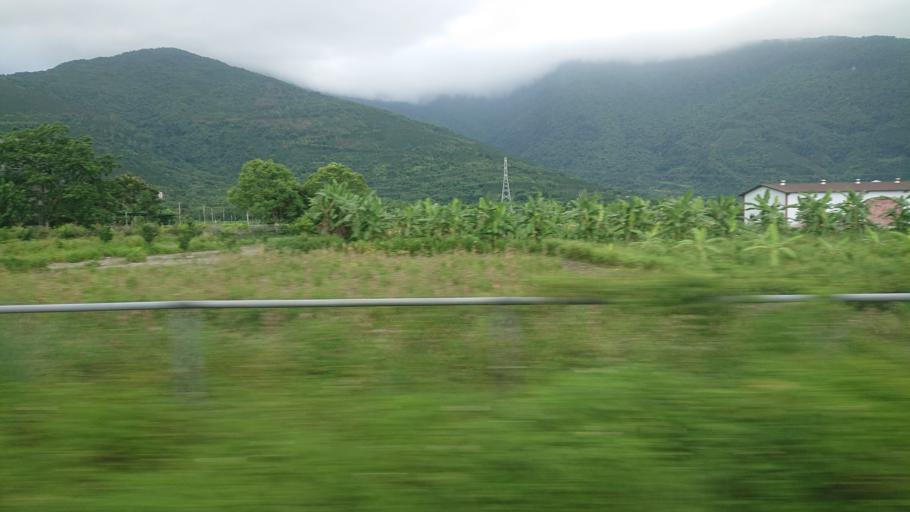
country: TW
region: Taiwan
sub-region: Hualien
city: Hualian
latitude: 23.7404
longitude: 121.4438
